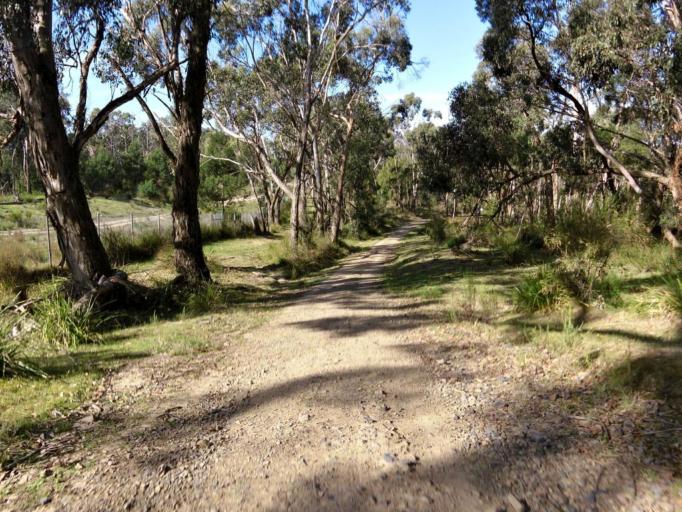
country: AU
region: Victoria
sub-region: Knox
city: Rowville
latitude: -37.9452
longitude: 145.2590
